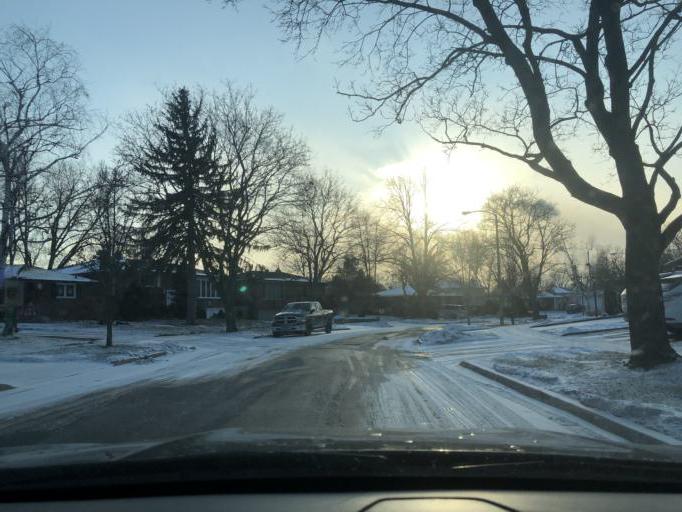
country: CA
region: Ontario
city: Scarborough
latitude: 43.7834
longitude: -79.1465
